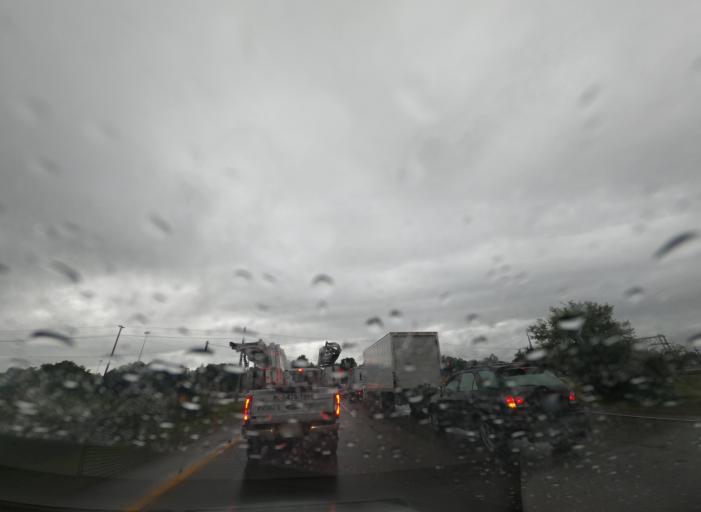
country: US
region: Kentucky
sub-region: Jefferson County
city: Valley Station
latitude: 38.0934
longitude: -85.8745
